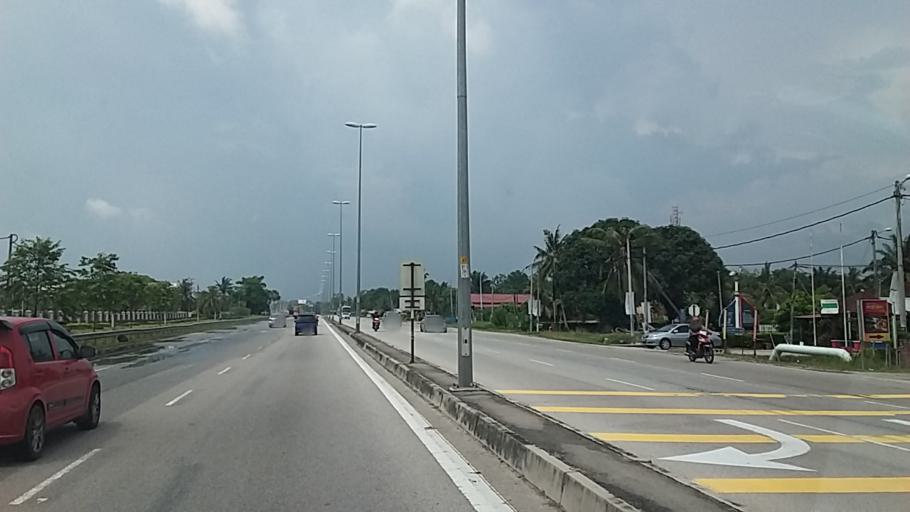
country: MY
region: Johor
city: Parit Raja
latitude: 1.8531
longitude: 103.0887
